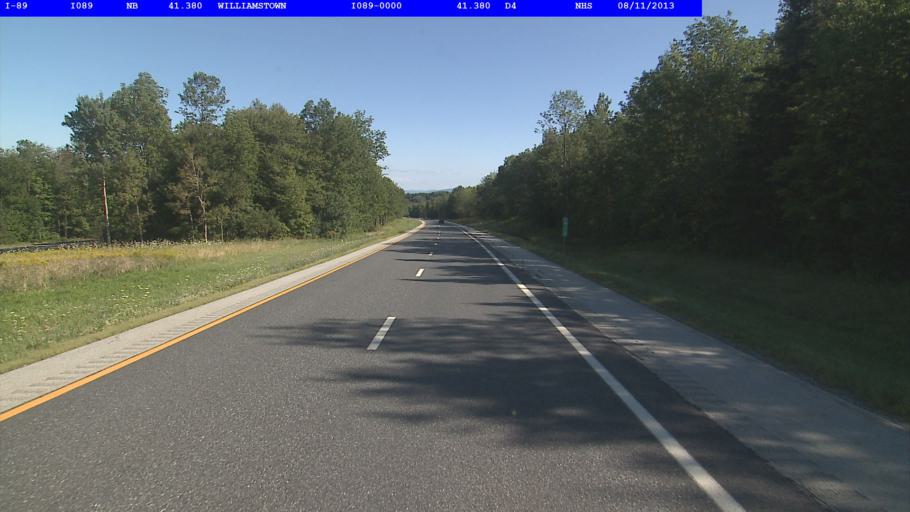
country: US
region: Vermont
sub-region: Washington County
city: Northfield
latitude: 44.0929
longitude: -72.6120
